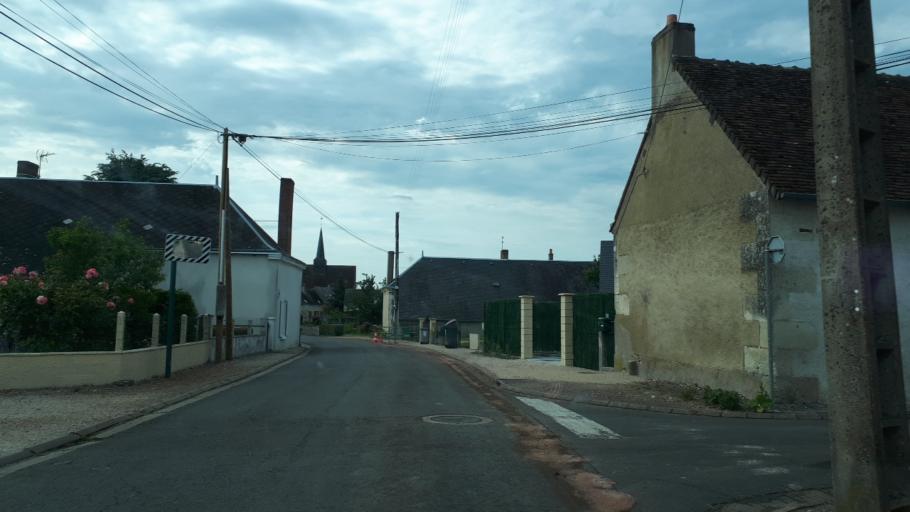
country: FR
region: Centre
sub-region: Departement du Loir-et-Cher
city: Saint-Amand-Longpre
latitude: 47.7248
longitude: 1.0082
